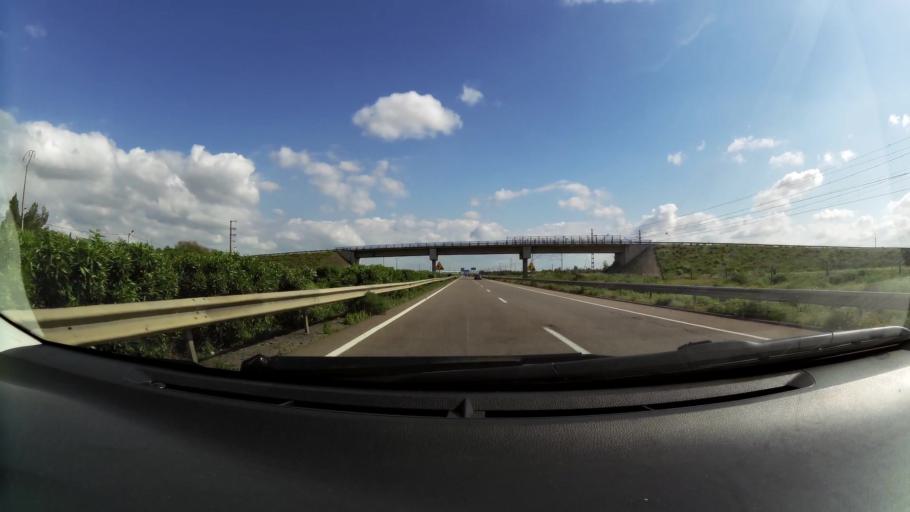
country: MA
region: Chaouia-Ouardigha
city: Nouaseur
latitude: 33.3335
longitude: -7.6097
